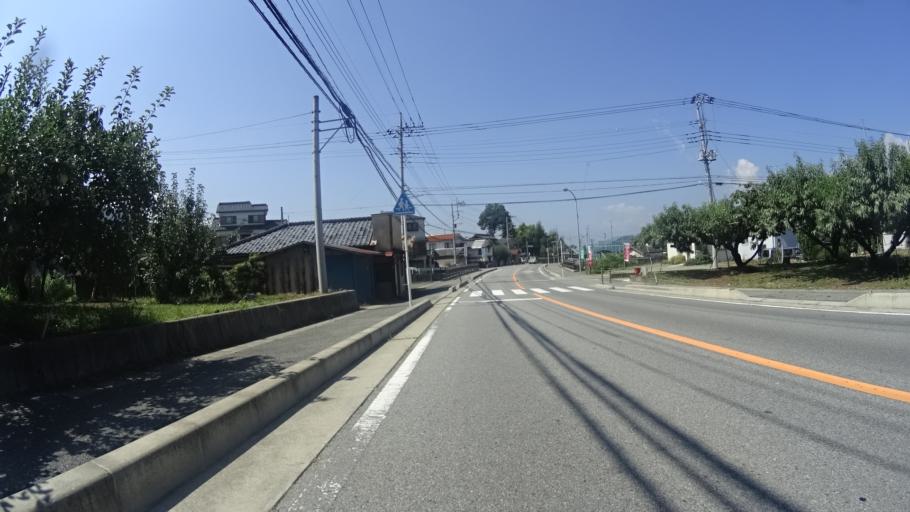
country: JP
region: Yamanashi
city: Enzan
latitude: 35.7229
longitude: 138.7535
